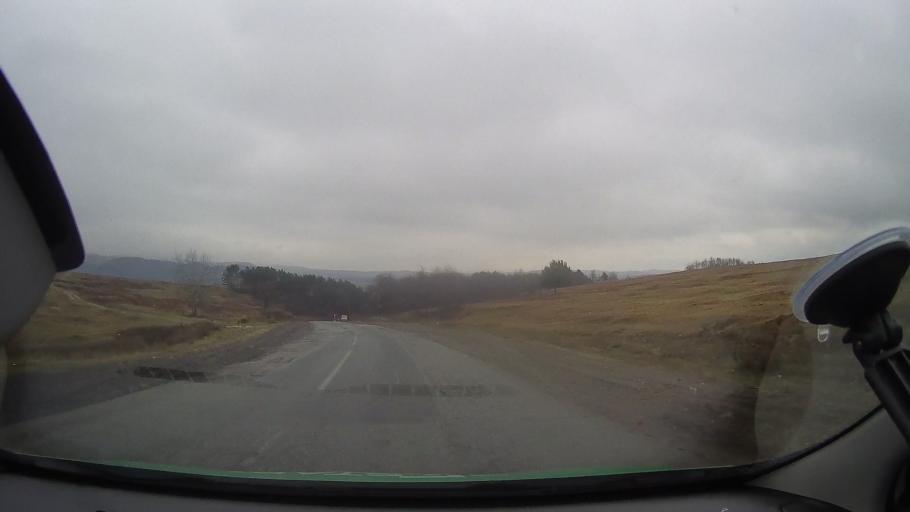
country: RO
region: Arad
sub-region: Comuna Halmagiu
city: Halmagiu
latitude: 46.2814
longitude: 22.5853
